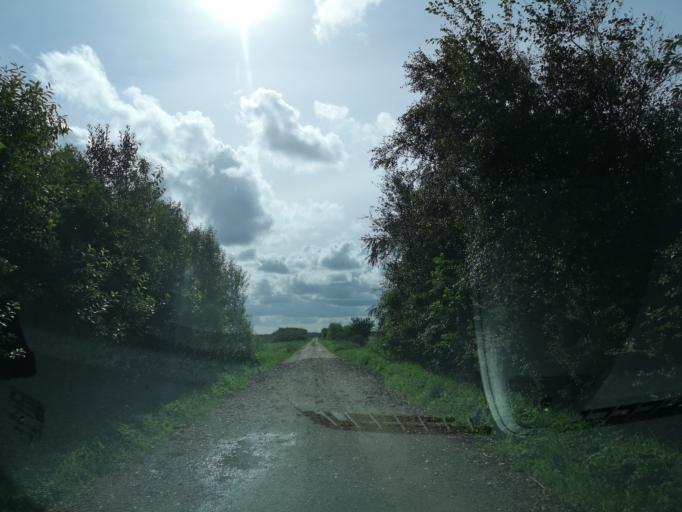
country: DK
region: Central Jutland
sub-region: Ringkobing-Skjern Kommune
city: Tarm
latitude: 55.9404
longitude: 8.5371
